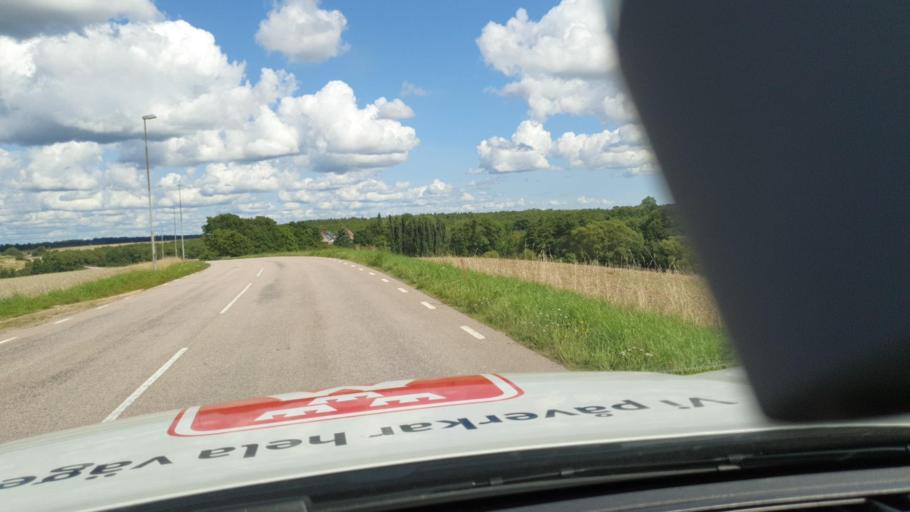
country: SE
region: Skane
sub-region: Astorps Kommun
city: Kvidinge
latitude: 56.1292
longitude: 13.0876
